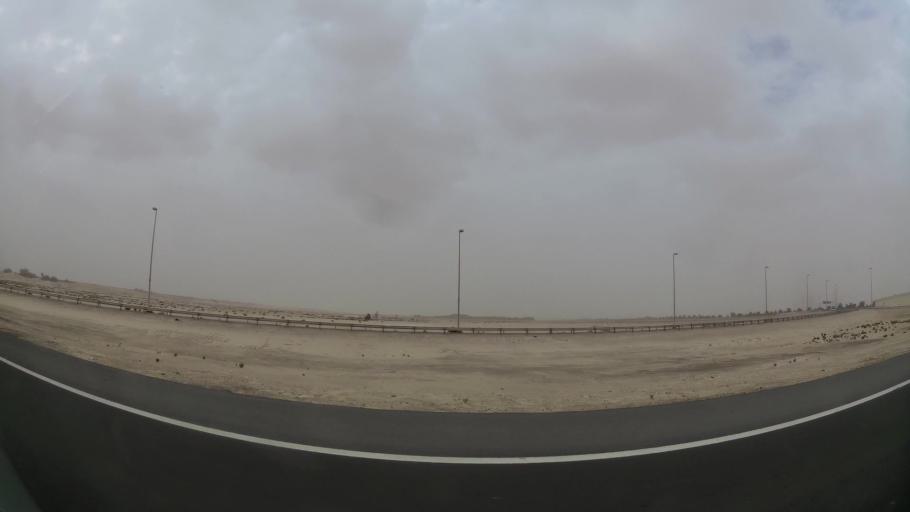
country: AE
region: Abu Dhabi
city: Abu Dhabi
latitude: 24.4100
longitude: 54.7153
